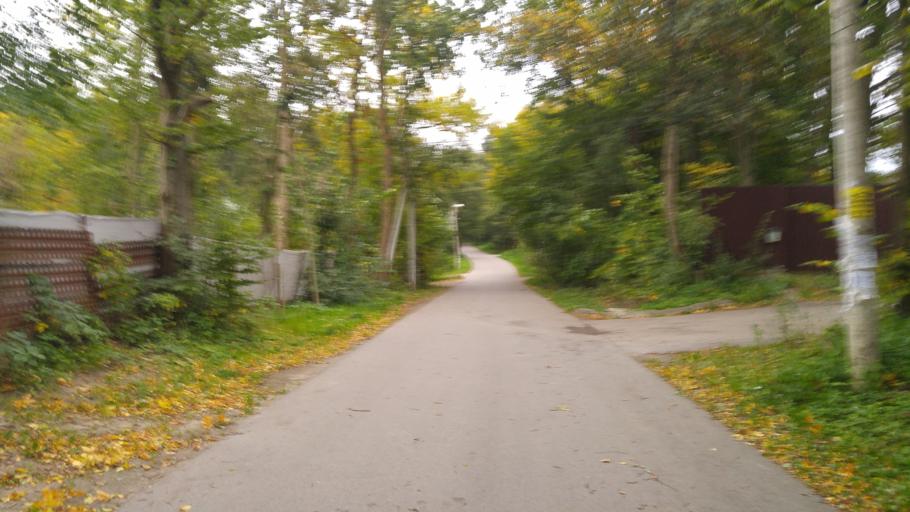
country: RU
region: Kaliningrad
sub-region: Gorod Kaliningrad
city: Kaliningrad
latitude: 54.7289
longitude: 20.4513
